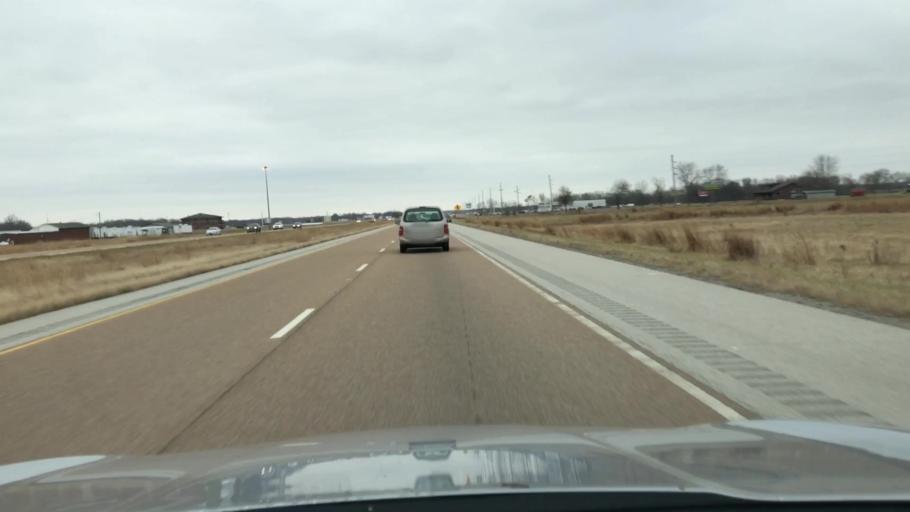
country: US
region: Illinois
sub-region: Macoupin County
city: Staunton
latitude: 39.0195
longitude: -89.7499
